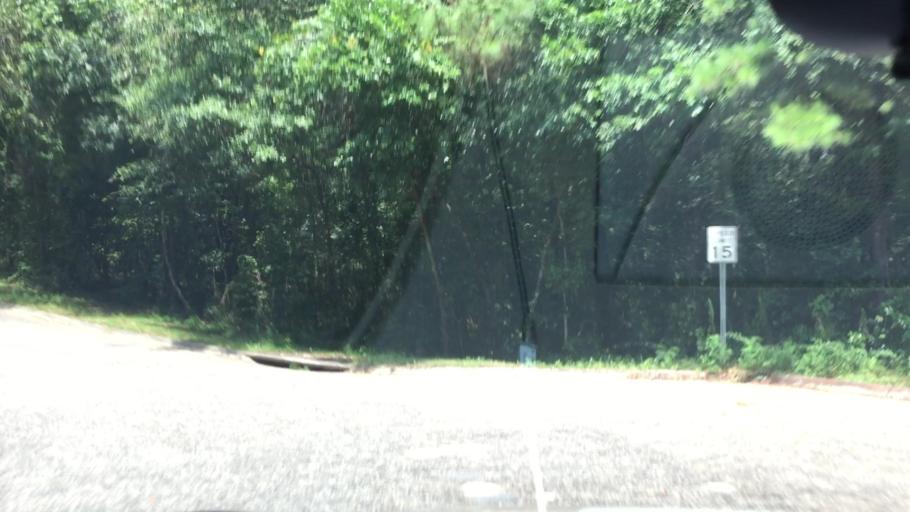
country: US
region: Alabama
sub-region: Coffee County
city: Enterprise
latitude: 31.3355
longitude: -85.8122
